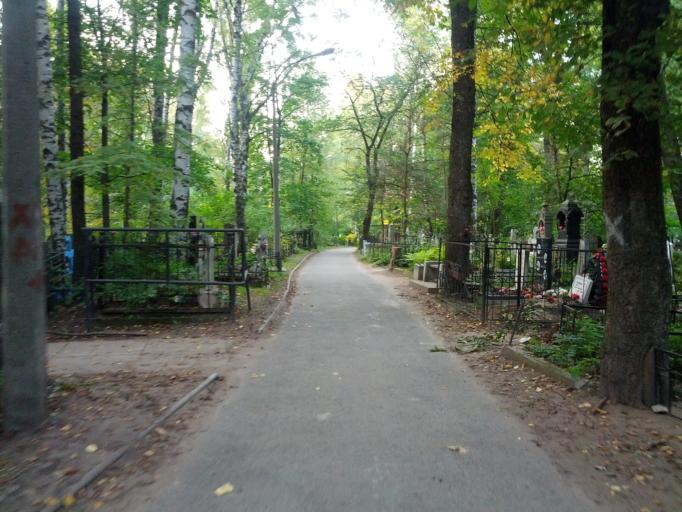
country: RU
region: St.-Petersburg
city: Krasnogvargeisky
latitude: 59.9470
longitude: 30.4288
